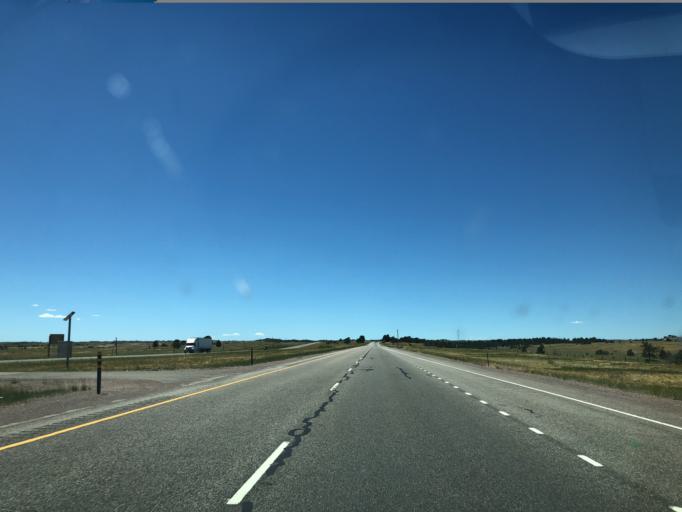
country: US
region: Wyoming
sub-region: Albany County
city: Laramie
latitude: 41.1257
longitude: -105.3120
